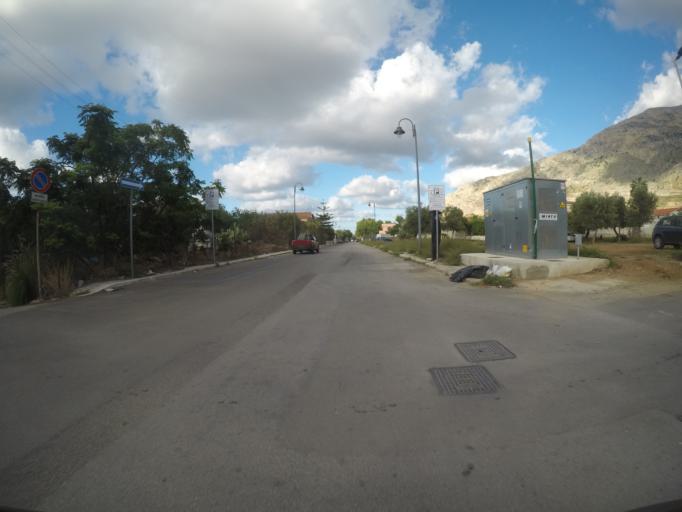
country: IT
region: Sicily
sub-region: Palermo
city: Isola delle Femmine
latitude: 38.1864
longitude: 13.2424
